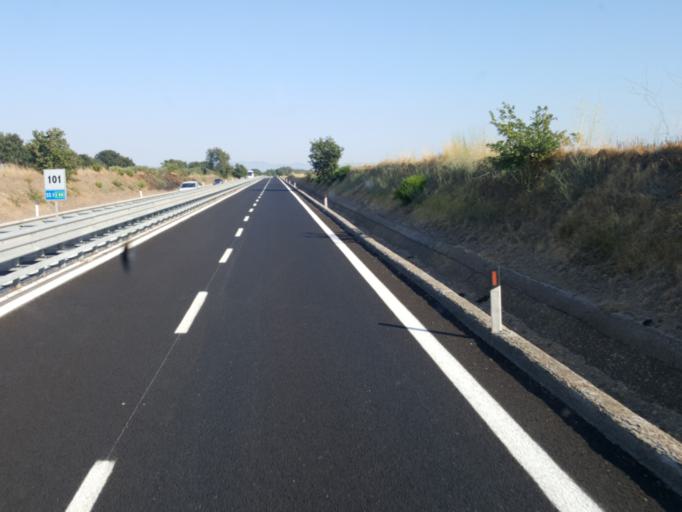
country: IT
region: Latium
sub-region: Provincia di Viterbo
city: Montalto di Castro
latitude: 42.3027
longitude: 11.6672
